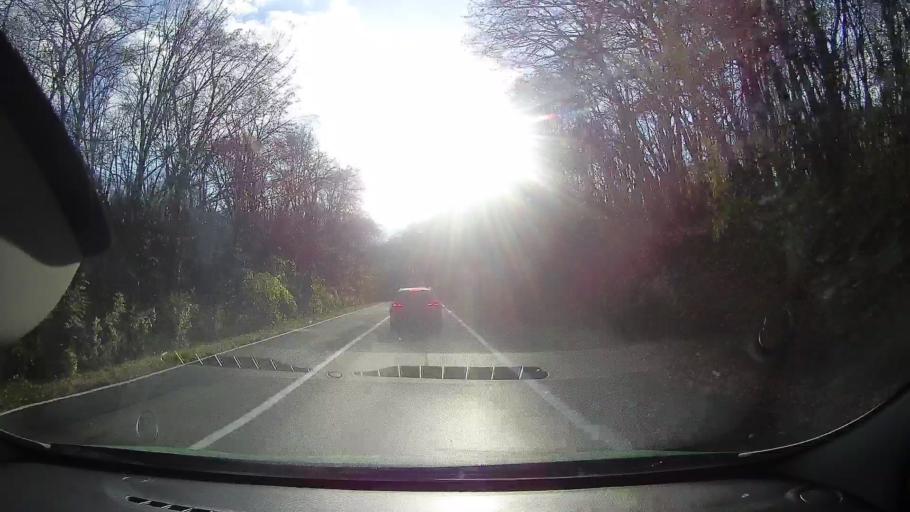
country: RO
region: Tulcea
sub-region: Comuna Topolog
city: Topolog
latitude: 44.9101
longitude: 28.4192
